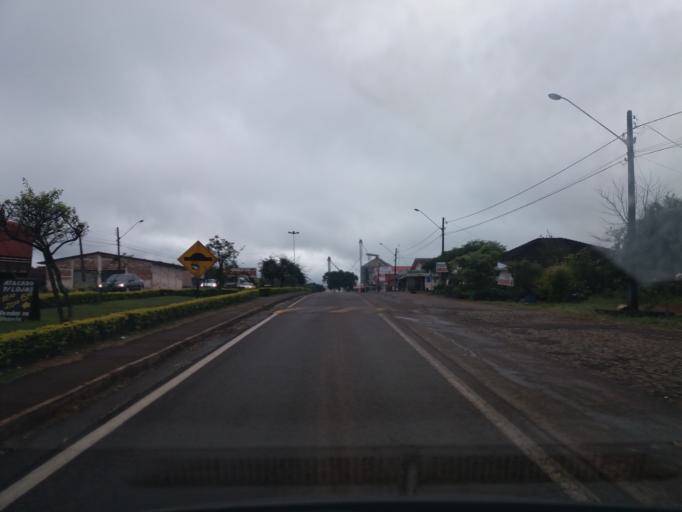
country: BR
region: Parana
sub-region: Cascavel
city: Cascavel
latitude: -25.2808
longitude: -53.5676
